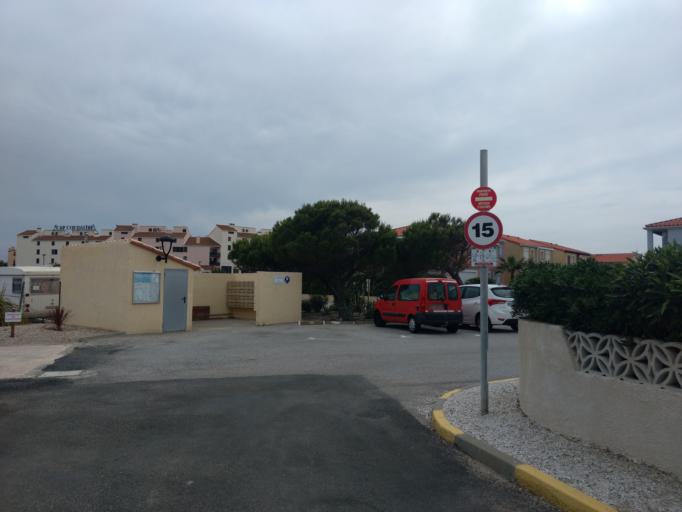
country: FR
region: Languedoc-Roussillon
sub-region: Departement des Pyrenees-Orientales
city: Le Barcares
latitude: 42.8164
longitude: 3.0224
